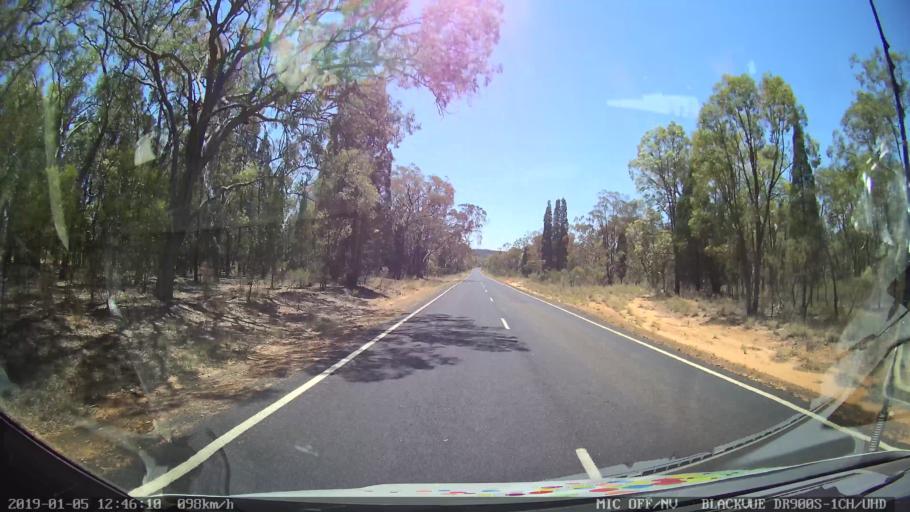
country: AU
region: New South Wales
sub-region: Warrumbungle Shire
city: Coonabarabran
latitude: -31.1207
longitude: 149.5590
